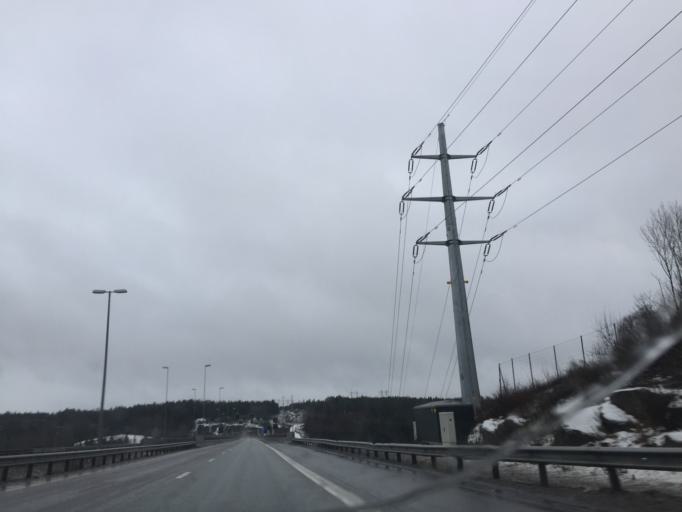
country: NO
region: Akershus
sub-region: Vestby
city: Vestby
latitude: 59.5417
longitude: 10.7253
